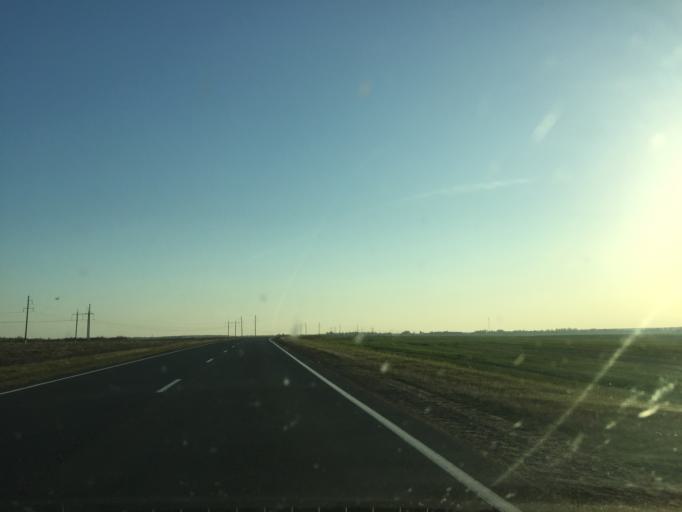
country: BY
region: Mogilev
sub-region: Mahilyowski Rayon
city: Kadino
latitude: 53.8325
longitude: 30.4782
